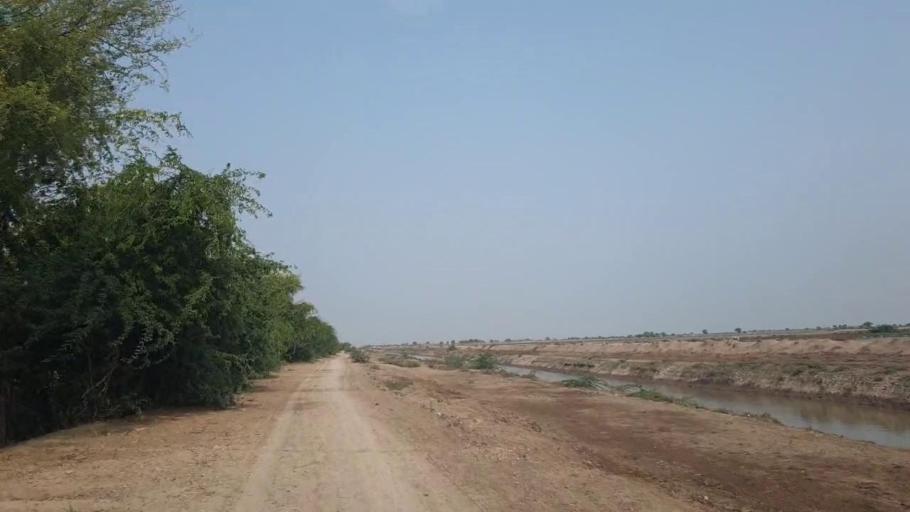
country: PK
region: Sindh
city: Badin
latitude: 24.7187
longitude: 68.7708
